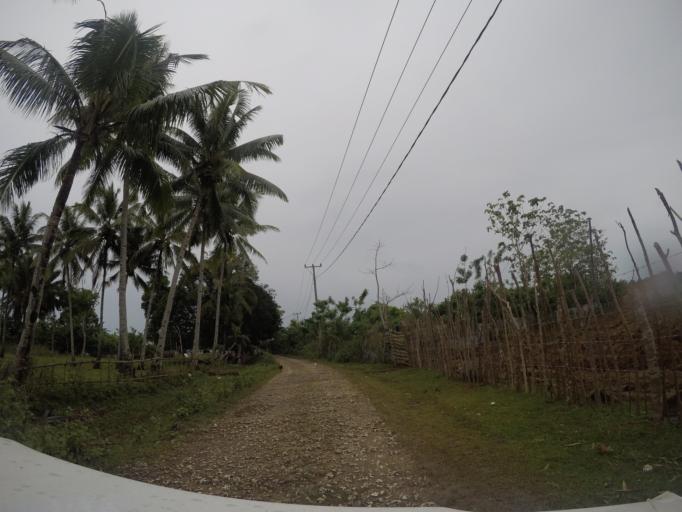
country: TL
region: Lautem
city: Lospalos
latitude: -8.5257
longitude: 127.0047
